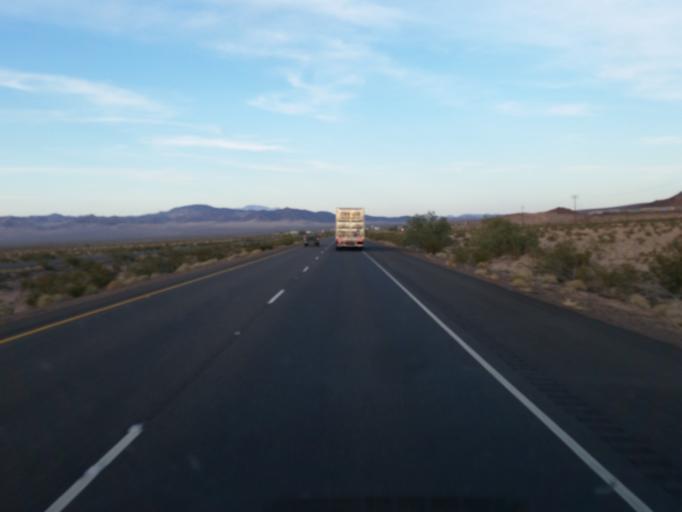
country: US
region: California
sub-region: San Bernardino County
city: Joshua Tree
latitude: 34.7240
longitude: -116.1916
